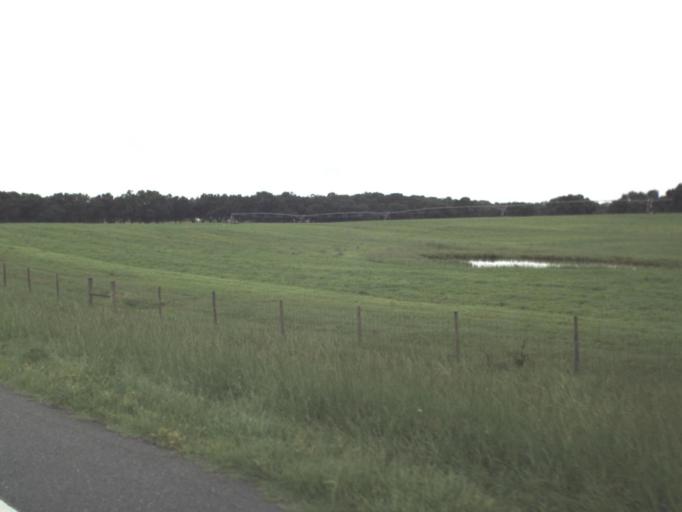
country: US
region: Florida
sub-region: Levy County
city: Williston
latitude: 29.2584
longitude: -82.4416
